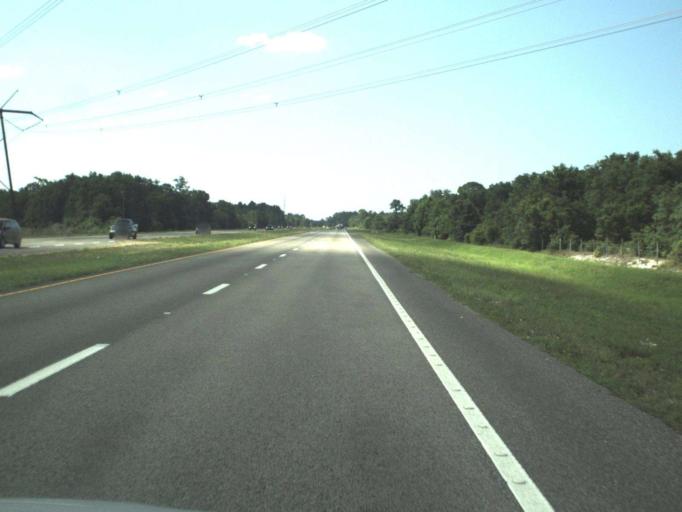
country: US
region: Florida
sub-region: Orange County
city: Christmas
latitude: 28.4128
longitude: -80.9522
